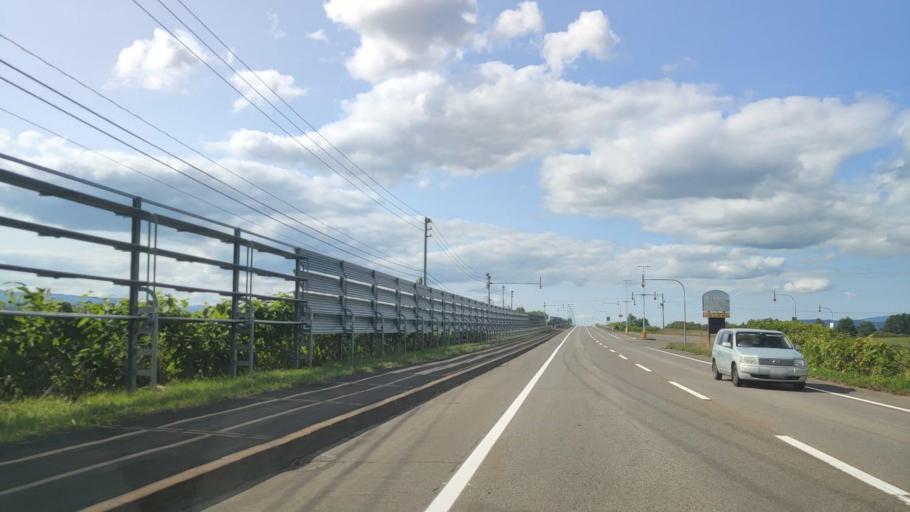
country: JP
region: Hokkaido
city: Nayoro
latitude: 44.4506
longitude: 142.3612
